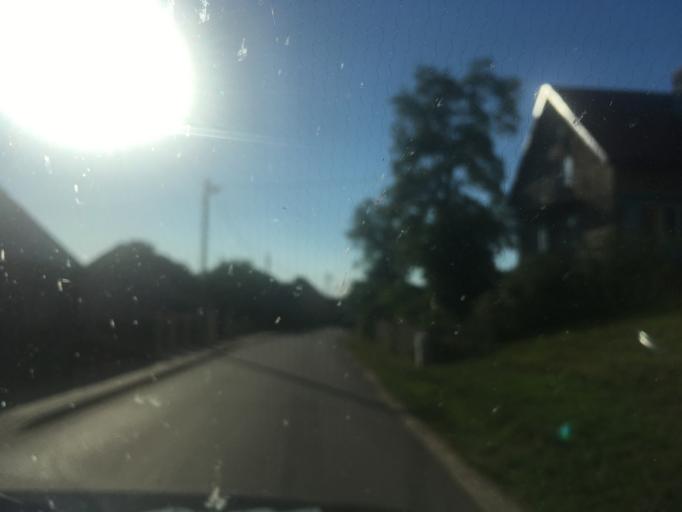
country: PL
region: Warmian-Masurian Voivodeship
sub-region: Powiat ostrodzki
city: Ostroda
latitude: 53.6770
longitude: 20.0463
